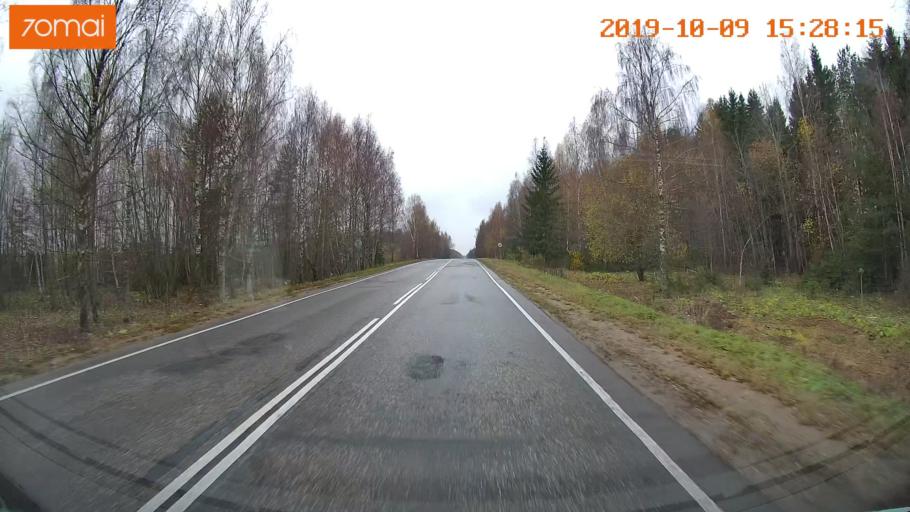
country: RU
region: Kostroma
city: Susanino
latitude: 58.0052
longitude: 41.3630
